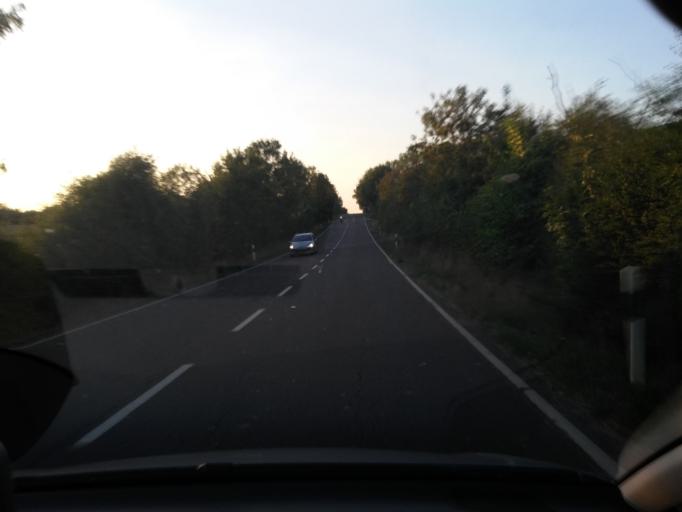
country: LU
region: Luxembourg
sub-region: Canton d'Esch-sur-Alzette
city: Frisange
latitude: 49.5259
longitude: 6.1837
